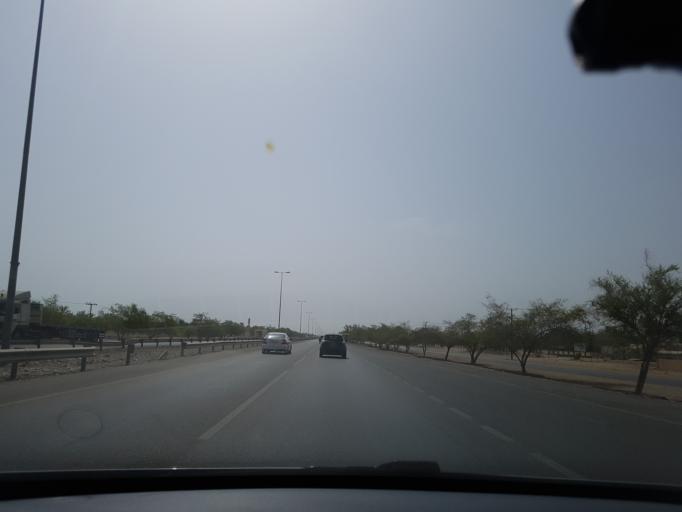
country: OM
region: Al Batinah
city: Al Khaburah
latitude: 23.9425
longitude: 57.1203
